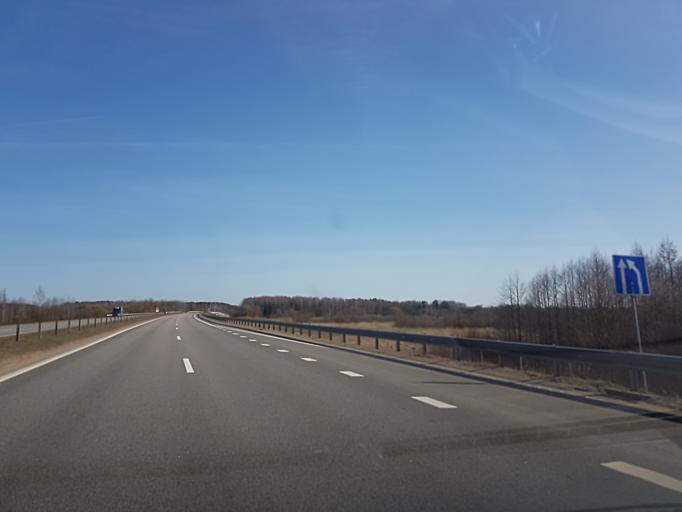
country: BY
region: Minsk
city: Pukhavichy
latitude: 53.5319
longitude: 28.2696
